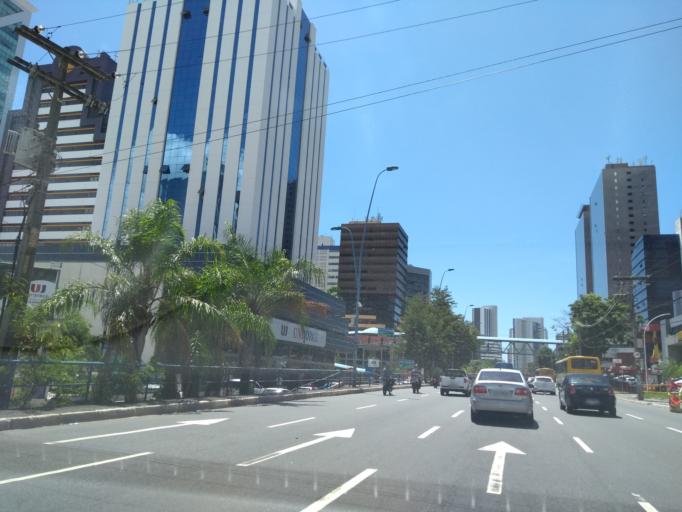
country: BR
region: Bahia
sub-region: Salvador
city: Salvador
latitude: -12.9817
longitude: -38.4554
